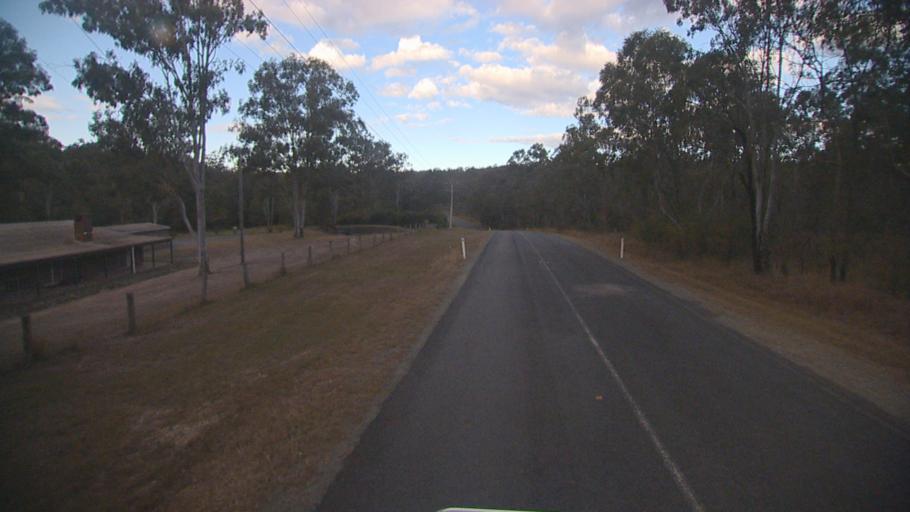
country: AU
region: Queensland
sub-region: Logan
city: Windaroo
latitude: -27.8142
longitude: 153.1604
